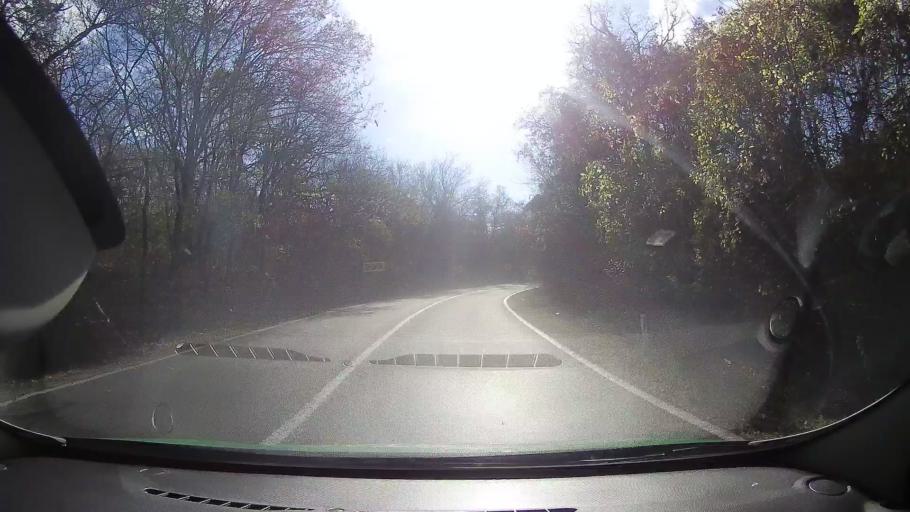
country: RO
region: Tulcea
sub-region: Oras Babadag
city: Babadag
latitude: 44.8462
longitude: 28.6997
